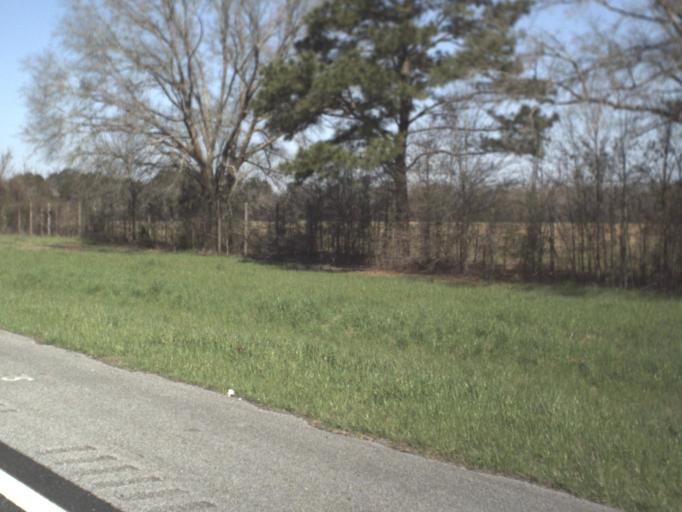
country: US
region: Florida
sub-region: Jackson County
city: Sneads
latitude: 30.6419
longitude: -85.0009
